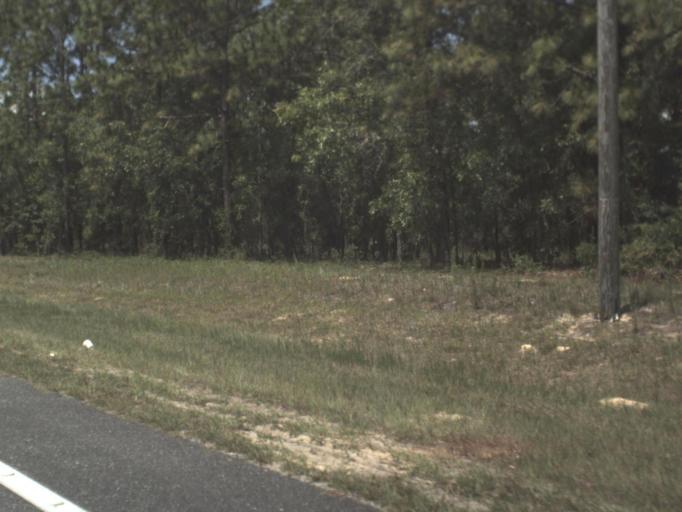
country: US
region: Florida
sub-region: Levy County
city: Williston Highlands
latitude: 29.3497
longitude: -82.5085
